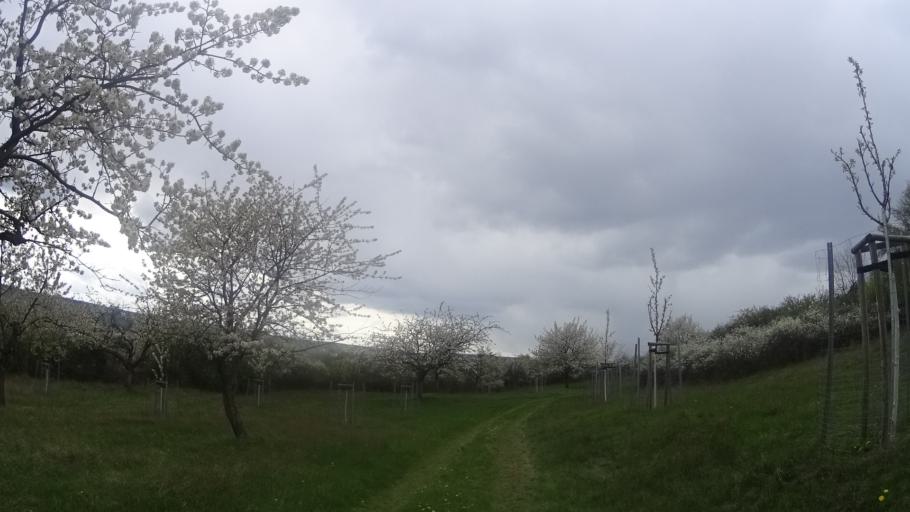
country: DE
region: Thuringia
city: Wandersleben
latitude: 50.8803
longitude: 10.8319
